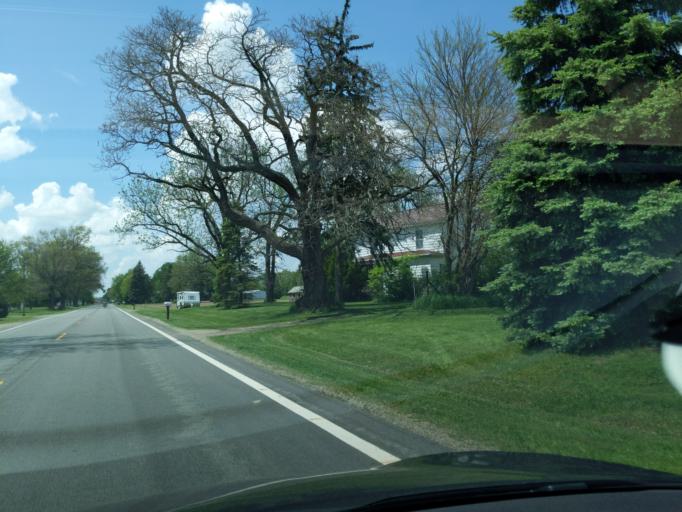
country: US
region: Michigan
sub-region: Ingham County
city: Stockbridge
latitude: 42.5077
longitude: -84.1530
